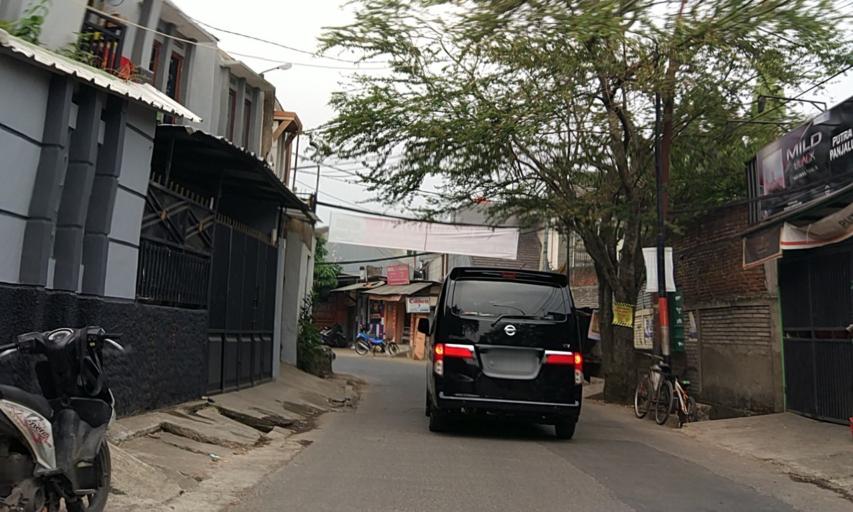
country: ID
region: West Java
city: Bandung
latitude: -6.9122
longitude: 107.6586
